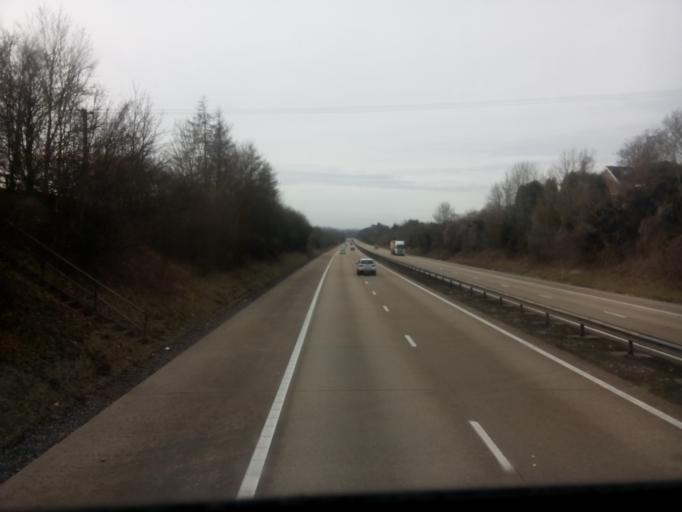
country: GB
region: England
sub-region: Hampshire
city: Overton
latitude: 51.1849
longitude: -1.2122
